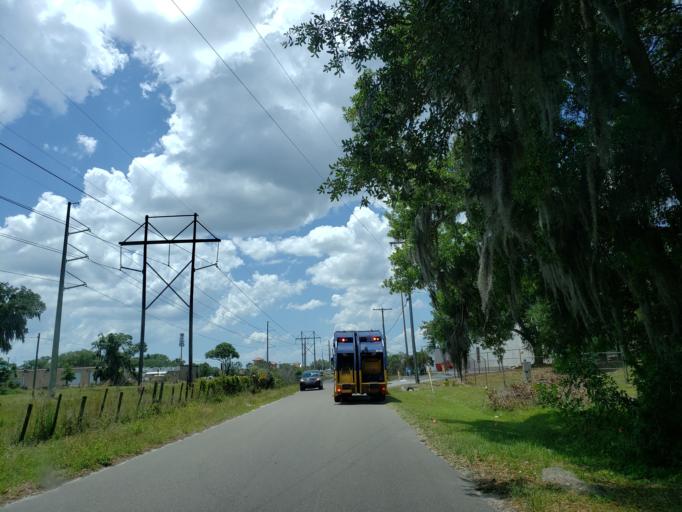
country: US
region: Florida
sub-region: Hillsborough County
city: Riverview
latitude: 27.8554
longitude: -82.3239
